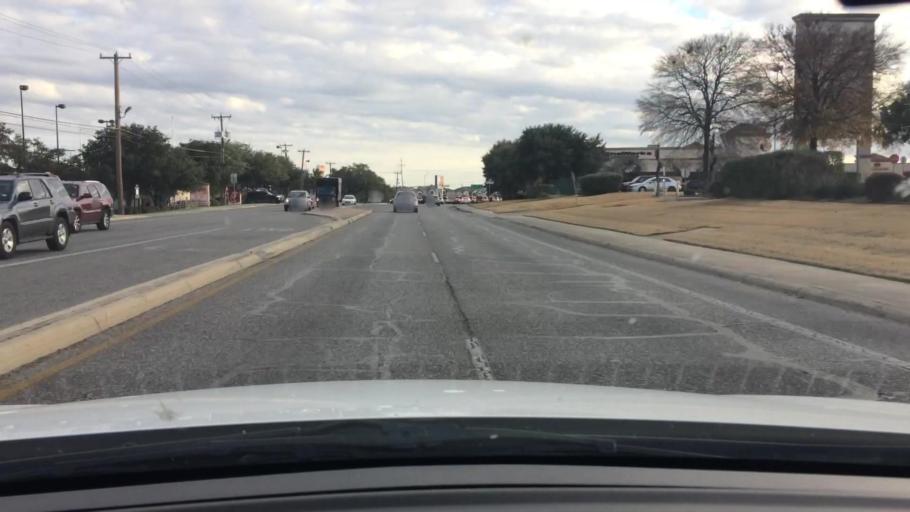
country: US
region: Texas
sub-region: Bexar County
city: Hollywood Park
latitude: 29.6117
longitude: -98.5088
